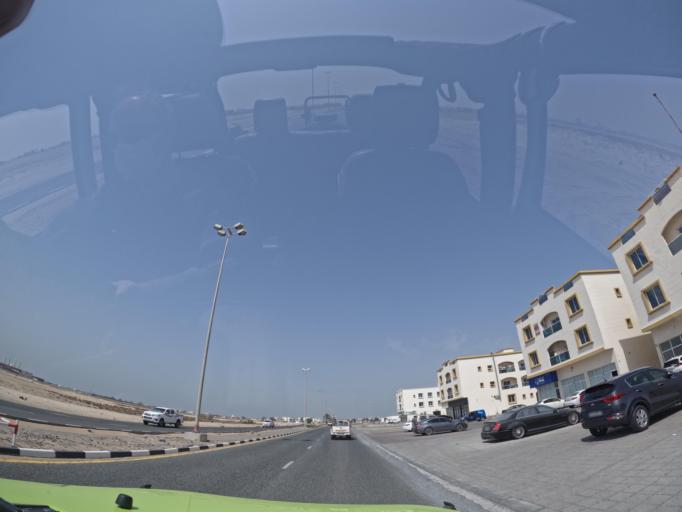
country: AE
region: Umm al Qaywayn
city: Umm al Qaywayn
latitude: 25.5197
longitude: 55.5546
